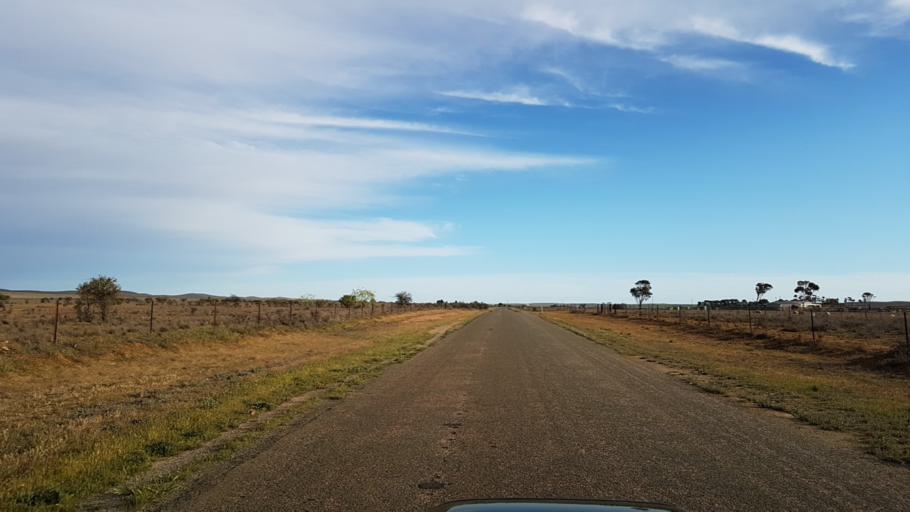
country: AU
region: South Australia
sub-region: Peterborough
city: Peterborough
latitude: -32.9847
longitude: 138.8507
